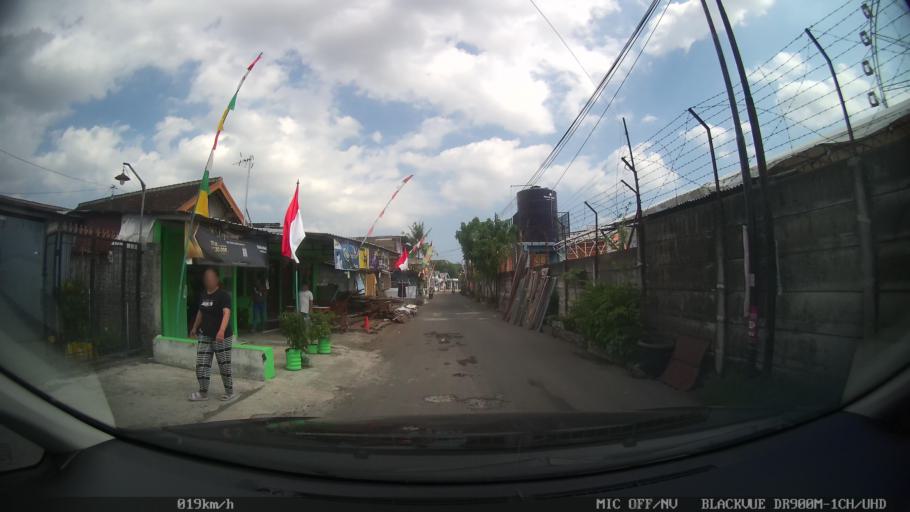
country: ID
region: Daerah Istimewa Yogyakarta
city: Yogyakarta
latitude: -7.7671
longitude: 110.3561
